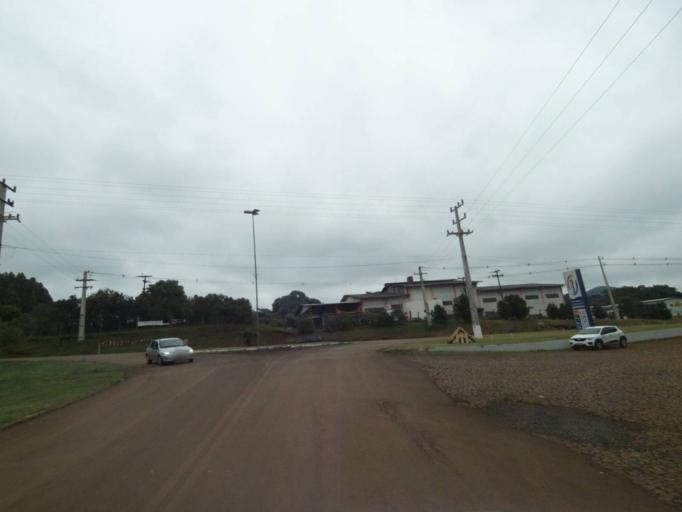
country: BR
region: Parana
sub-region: Pitanga
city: Pitanga
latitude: -24.9286
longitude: -51.8742
